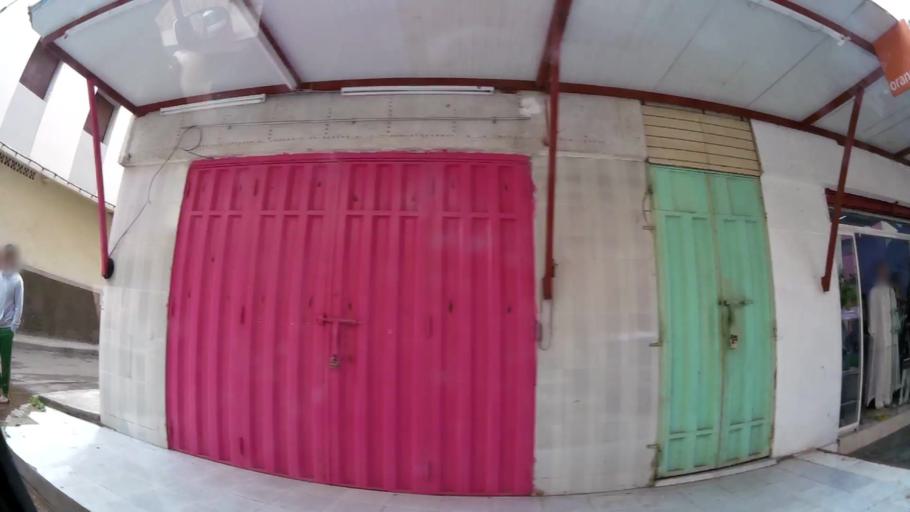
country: MA
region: Grand Casablanca
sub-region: Mediouna
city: Tit Mellil
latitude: 33.6086
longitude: -7.5164
